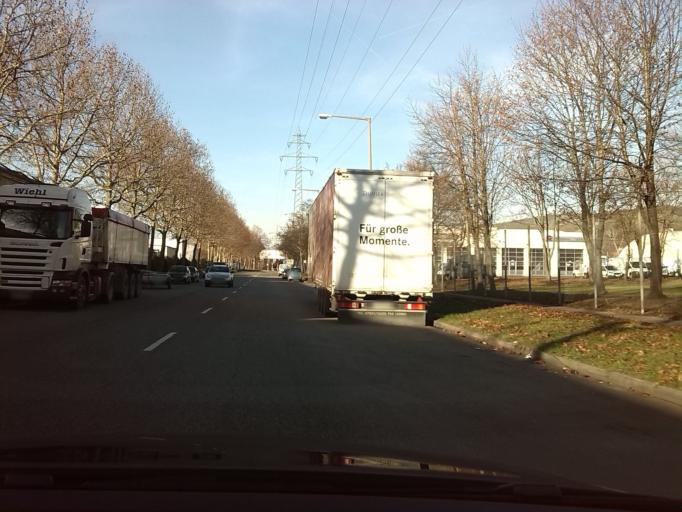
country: DE
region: Baden-Wuerttemberg
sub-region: Regierungsbezirk Stuttgart
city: Ostfildern
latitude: 48.7597
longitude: 9.2672
